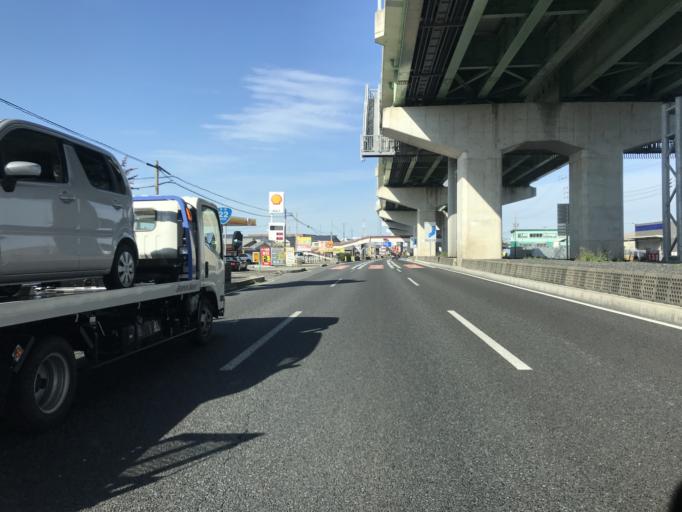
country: JP
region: Aichi
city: Iwakura
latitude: 35.2423
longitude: 136.8463
